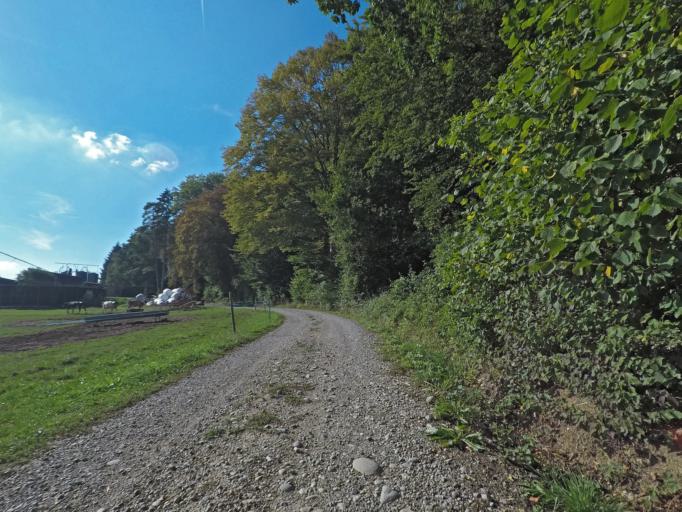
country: CH
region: Thurgau
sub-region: Frauenfeld District
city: Diessenhofen
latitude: 47.6532
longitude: 8.7379
